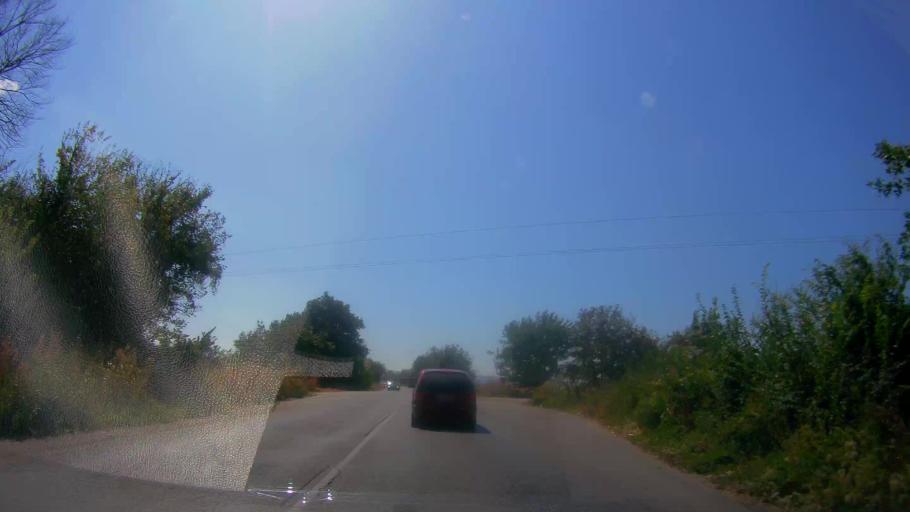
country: BG
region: Veliko Turnovo
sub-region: Obshtina Gorna Oryakhovitsa
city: Purvomaytsi
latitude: 43.2363
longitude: 25.6407
